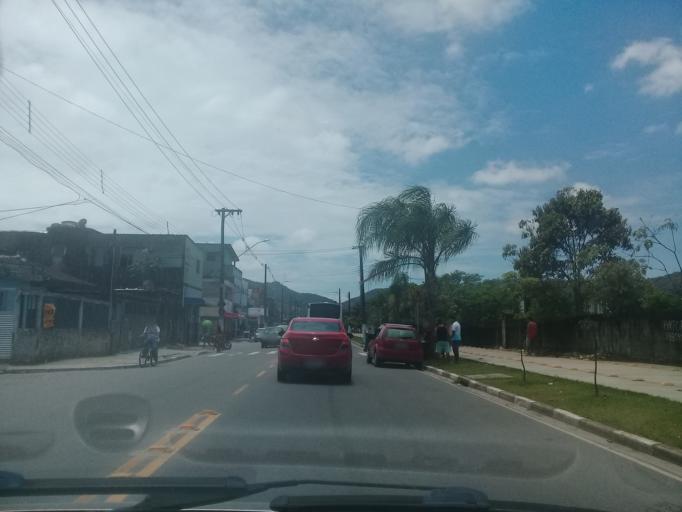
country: BR
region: Sao Paulo
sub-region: Guaruja
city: Guaruja
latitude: -23.9668
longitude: -46.2558
